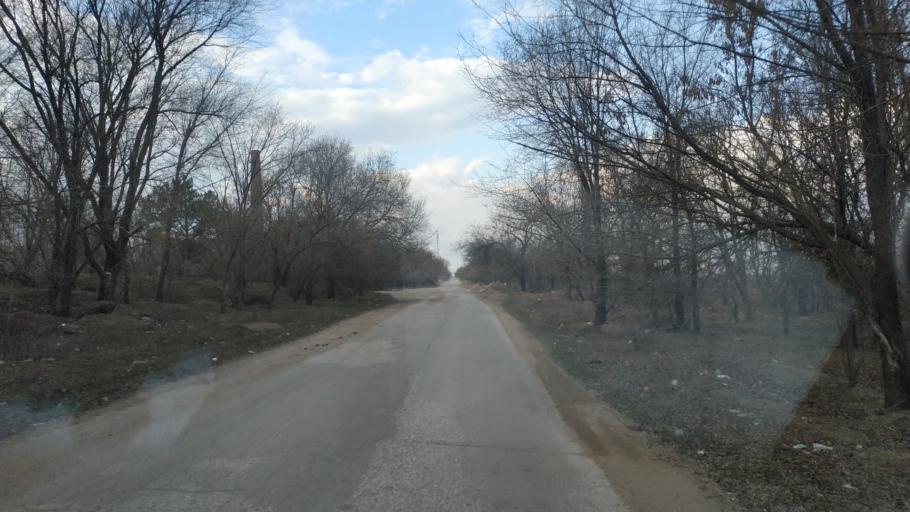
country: MD
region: Anenii Noi
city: Varnita
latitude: 46.8949
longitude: 29.4616
